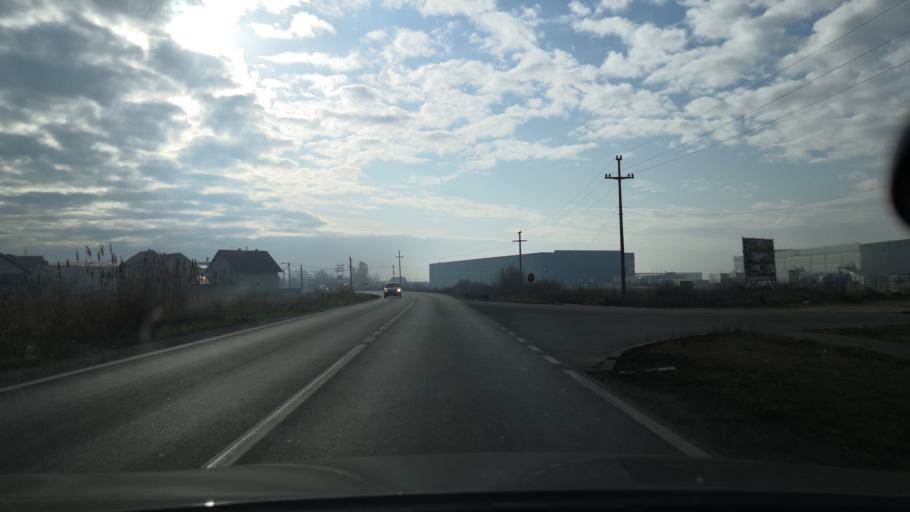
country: RS
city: Ugrinovci
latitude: 44.8547
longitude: 20.2053
